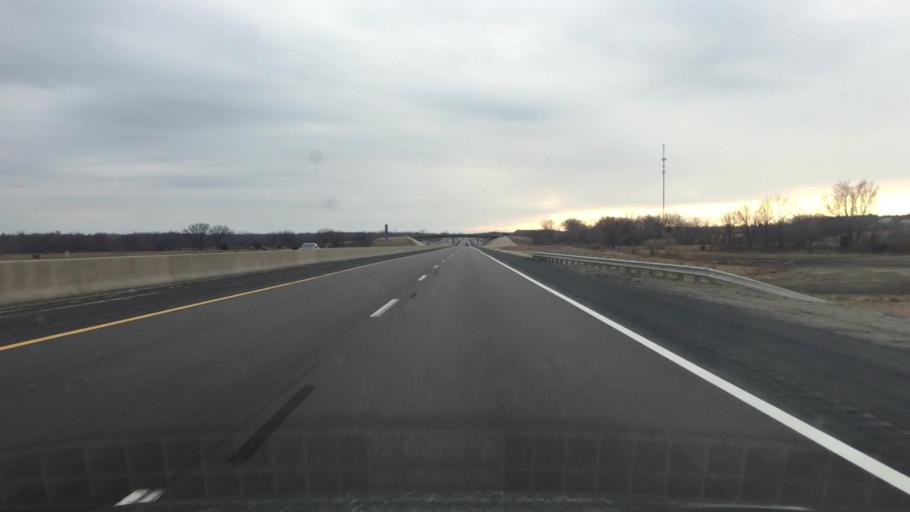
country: US
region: Kansas
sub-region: Osage County
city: Osage City
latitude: 38.7433
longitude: -95.9488
